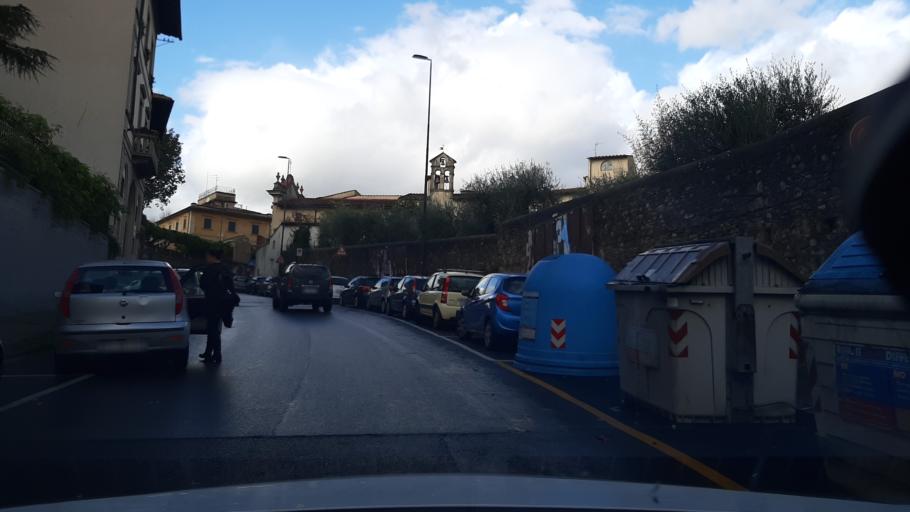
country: IT
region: Tuscany
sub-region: Province of Florence
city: Florence
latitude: 43.7900
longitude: 11.2625
